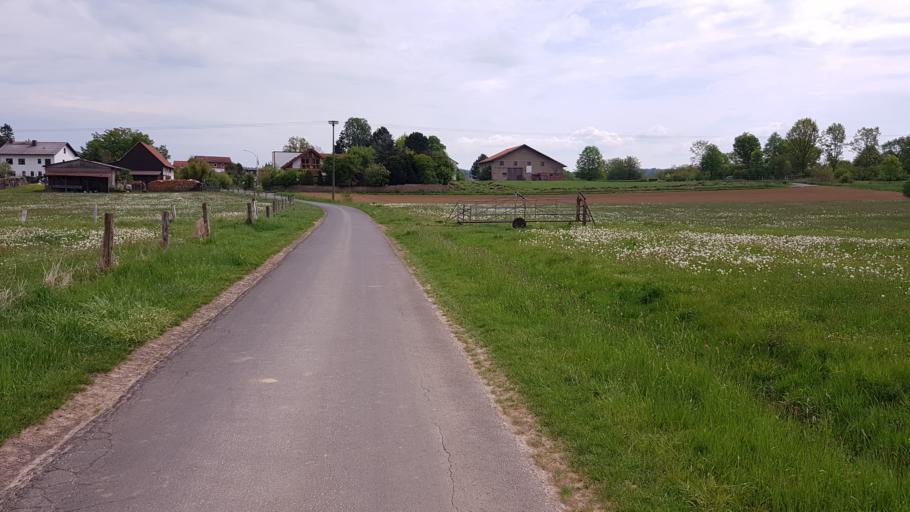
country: DE
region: Hesse
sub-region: Regierungsbezirk Giessen
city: Grunberg
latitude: 50.6478
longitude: 9.0222
